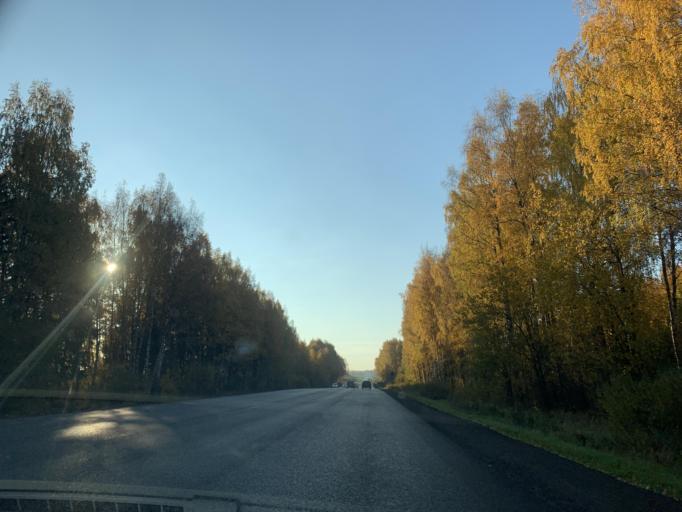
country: RU
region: Jaroslavl
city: Konstantinovskiy
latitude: 57.8043
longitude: 39.5902
